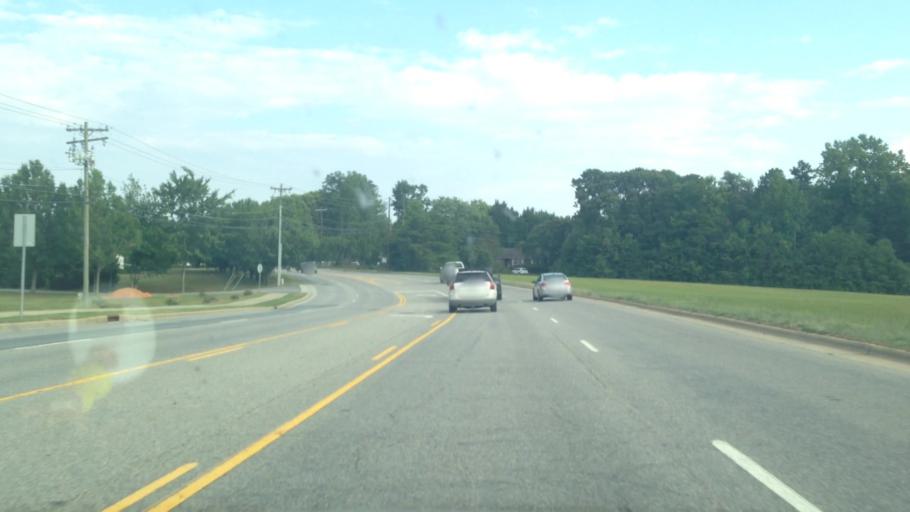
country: US
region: North Carolina
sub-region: Forsyth County
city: Kernersville
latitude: 36.0776
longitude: -80.0626
